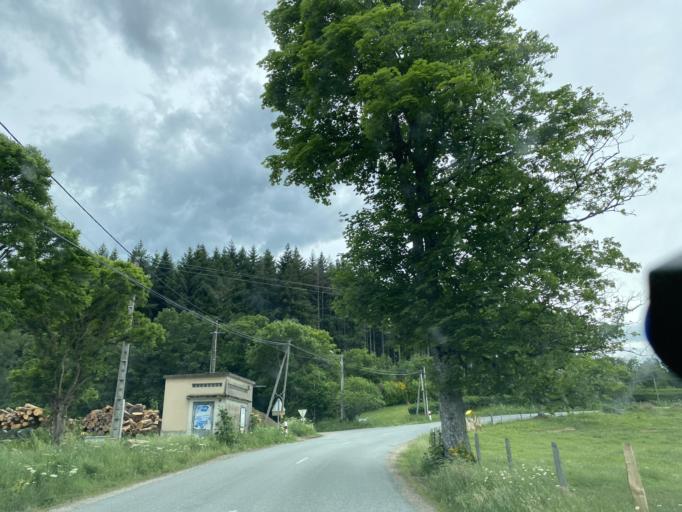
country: FR
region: Rhone-Alpes
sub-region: Departement de la Loire
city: Noiretable
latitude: 45.7952
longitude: 3.7240
